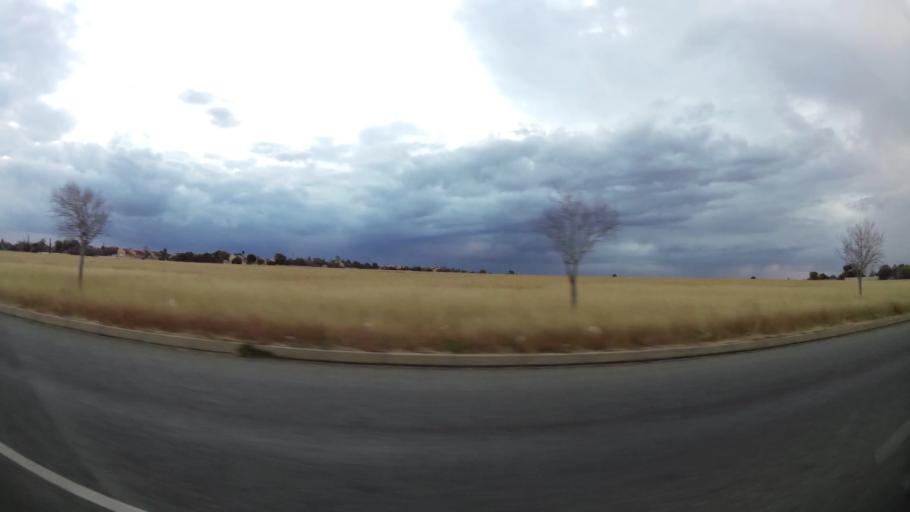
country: ZA
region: Orange Free State
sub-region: Lejweleputswa District Municipality
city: Welkom
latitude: -27.9561
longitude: 26.7544
